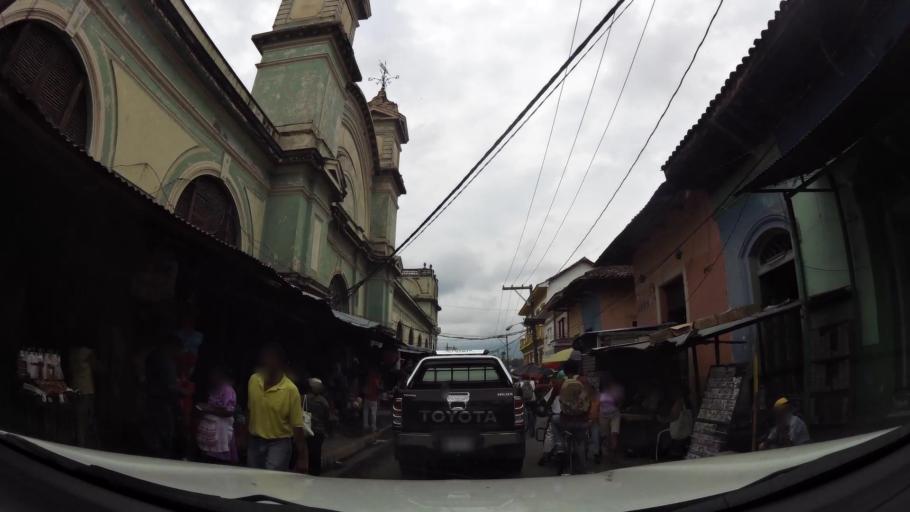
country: NI
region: Granada
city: Granada
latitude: 11.9269
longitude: -85.9552
